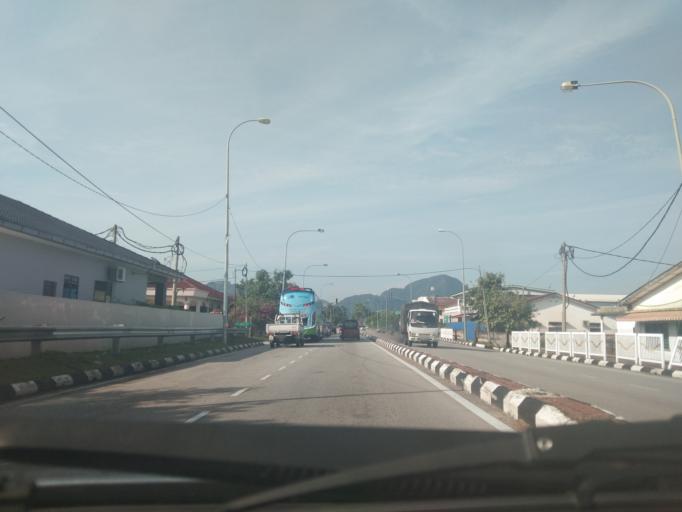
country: MY
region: Perak
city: Ipoh
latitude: 4.5877
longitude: 101.1274
